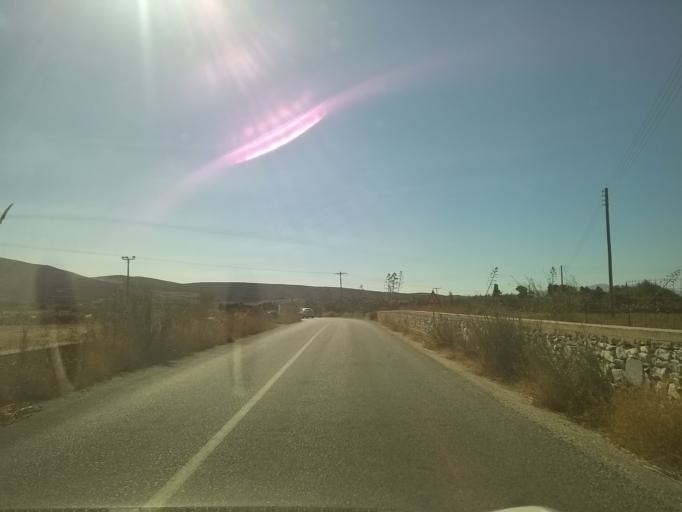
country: GR
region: South Aegean
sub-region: Nomos Kykladon
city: Filotion
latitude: 37.0442
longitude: 25.4263
